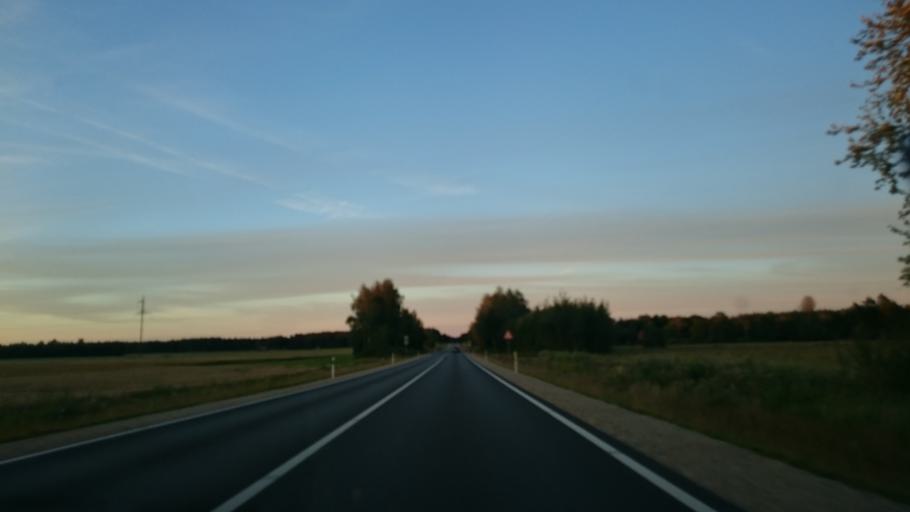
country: LV
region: Jaunpils
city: Jaunpils
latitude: 56.6782
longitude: 23.0909
